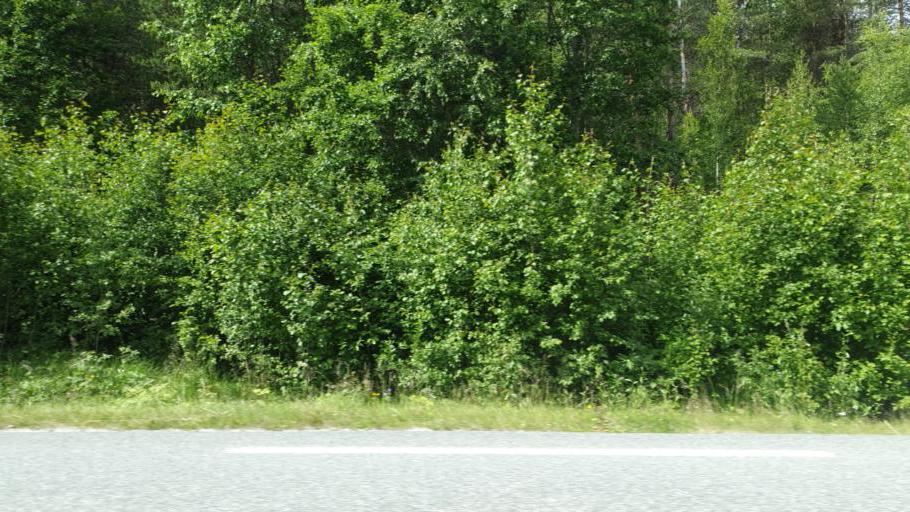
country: NO
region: Oppland
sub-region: Vaga
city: Vagamo
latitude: 61.7396
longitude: 9.0912
